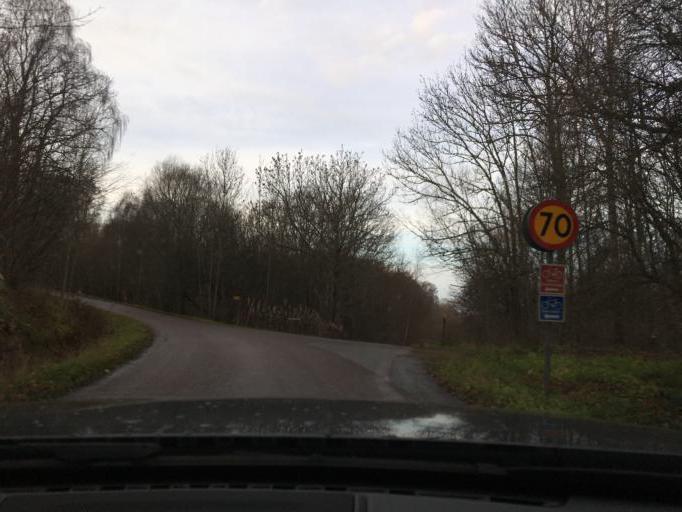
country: SE
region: Joenkoeping
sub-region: Jonkopings Kommun
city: Graenna
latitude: 57.9952
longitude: 14.4299
